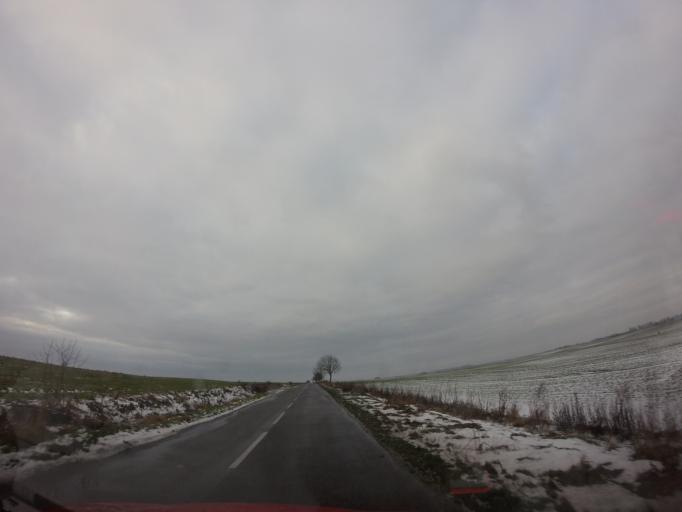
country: PL
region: West Pomeranian Voivodeship
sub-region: Powiat choszczenski
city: Pelczyce
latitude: 53.0513
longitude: 15.3715
